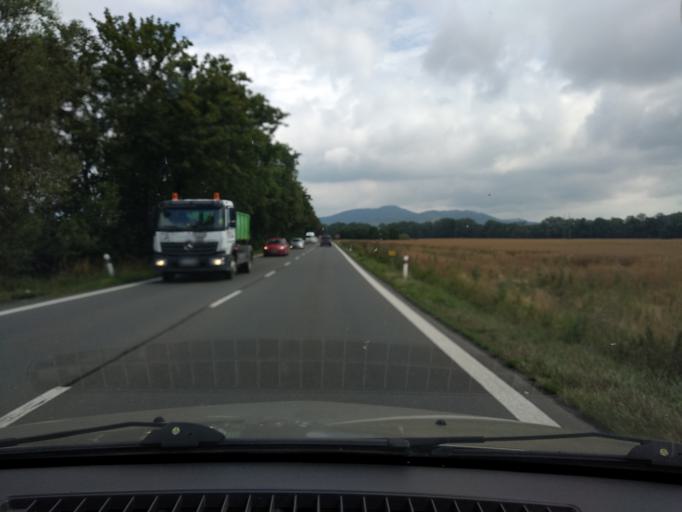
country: CZ
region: Olomoucky
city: Postrelmov
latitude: 49.9199
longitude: 16.9180
